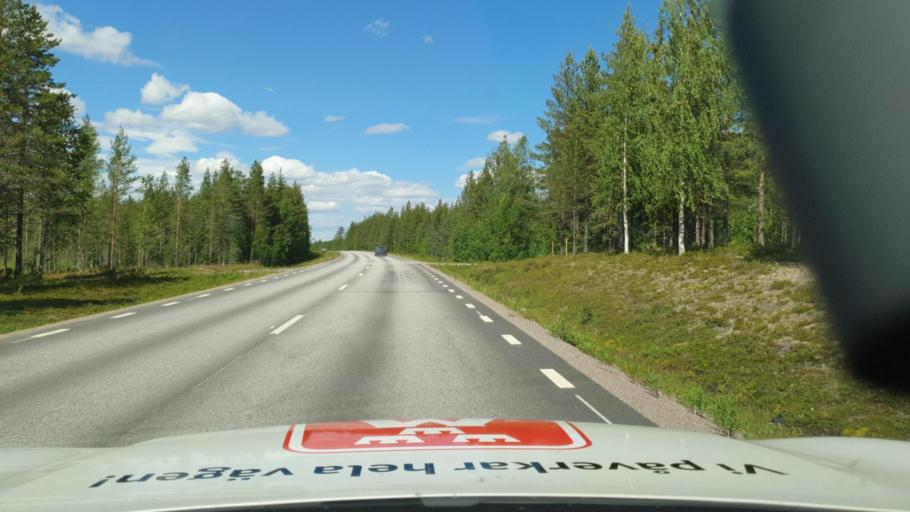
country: SE
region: Vaesterbotten
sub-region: Skelleftea Kommun
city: Langsele
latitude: 64.9818
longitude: 20.2296
